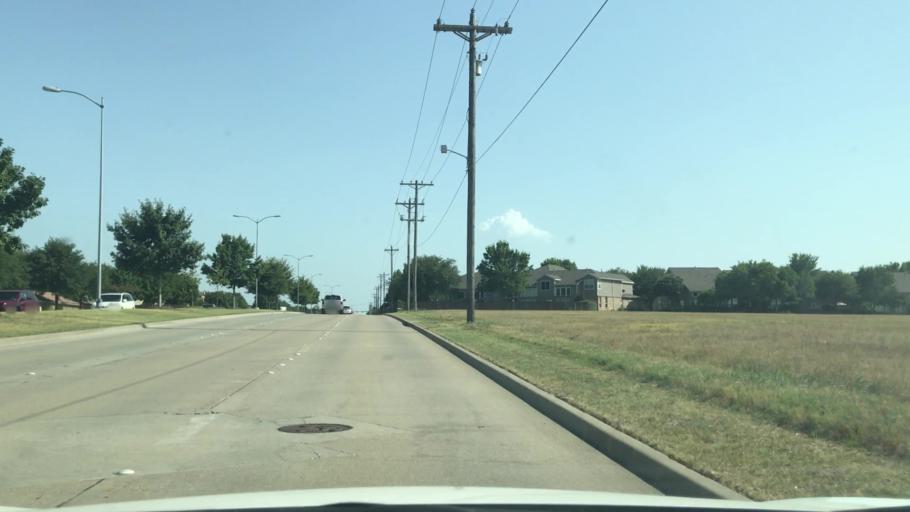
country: US
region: Texas
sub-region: Collin County
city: Frisco
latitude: 33.1170
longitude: -96.7509
